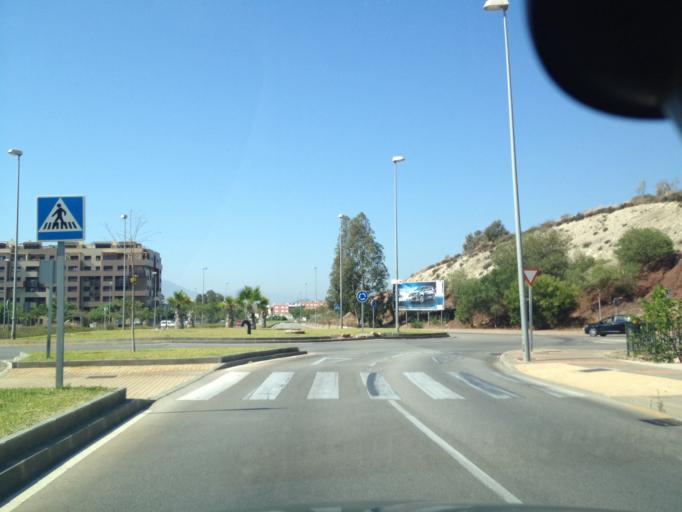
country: ES
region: Andalusia
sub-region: Provincia de Malaga
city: Malaga
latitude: 36.7259
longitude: -4.4844
